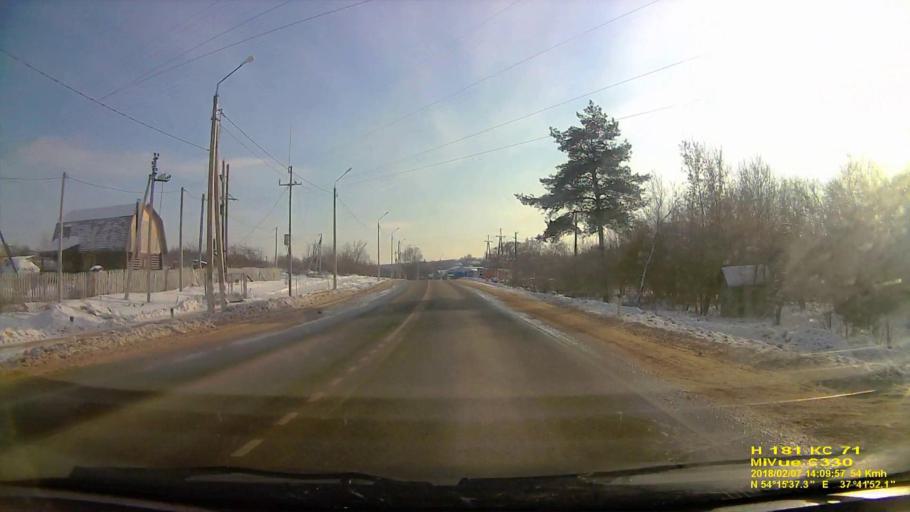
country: RU
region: Tula
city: Gorelki
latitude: 54.2603
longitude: 37.6977
